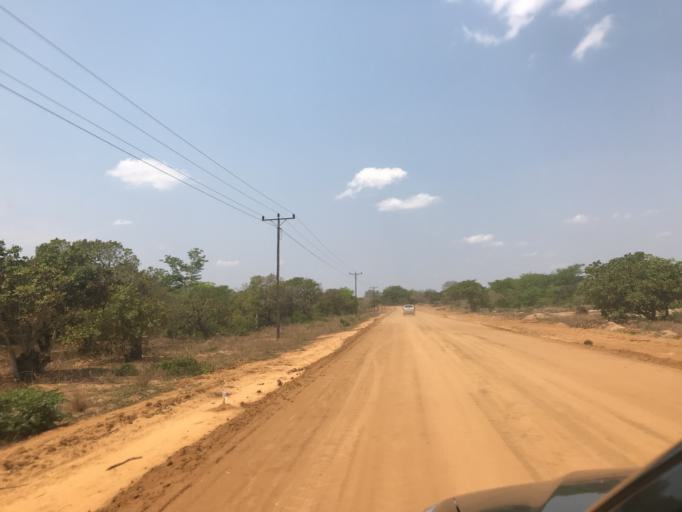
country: MZ
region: Gaza
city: Manjacaze
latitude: -24.5677
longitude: 33.9207
